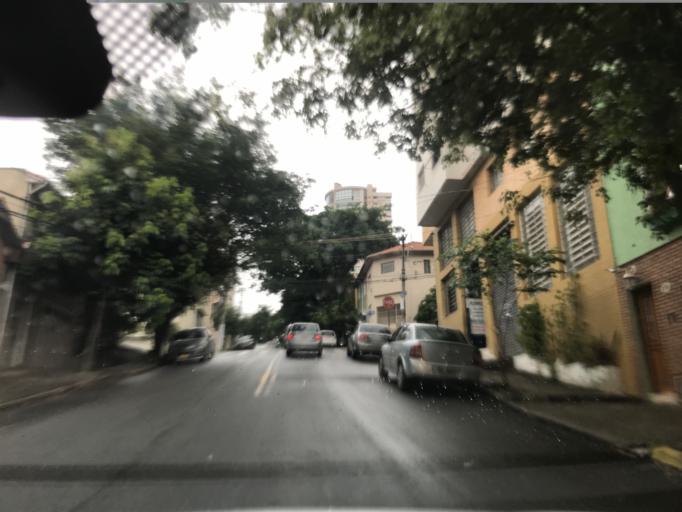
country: BR
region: Sao Paulo
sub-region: Sao Paulo
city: Sao Paulo
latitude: -23.5358
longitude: -46.6749
